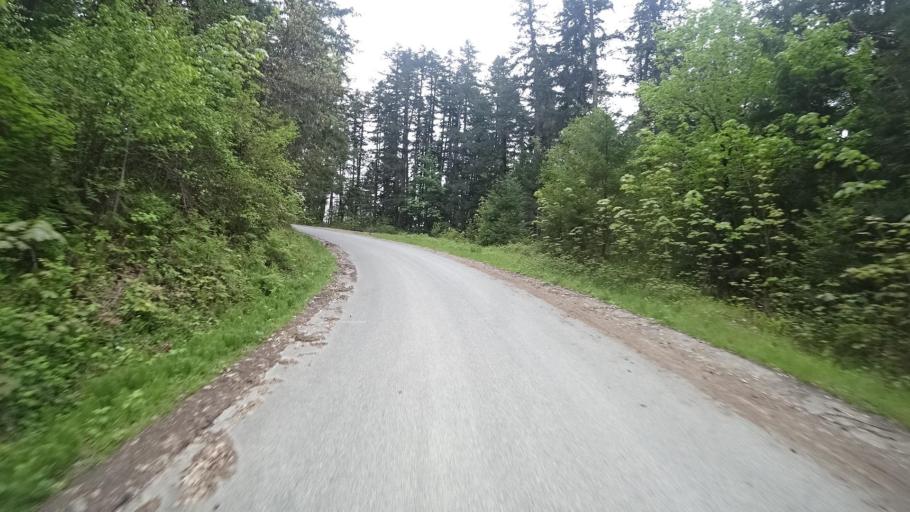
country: US
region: California
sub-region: Humboldt County
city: Willow Creek
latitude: 41.1241
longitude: -123.7481
